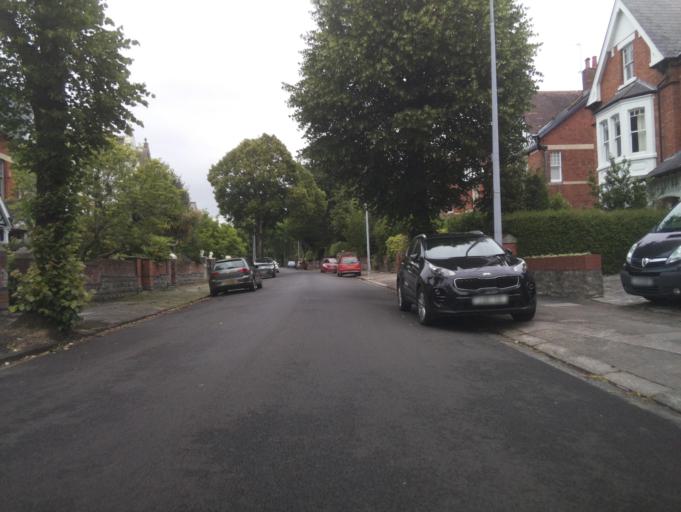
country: GB
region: Wales
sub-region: Vale of Glamorgan
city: Penarth
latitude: 51.4315
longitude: -3.1728
